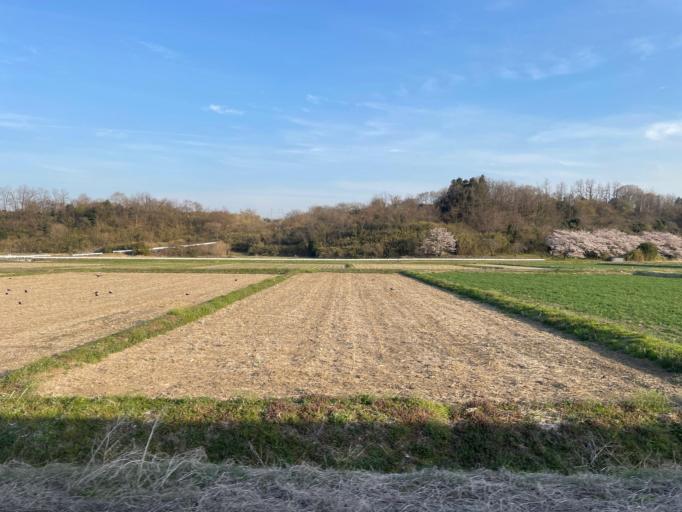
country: JP
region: Gunma
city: Annaka
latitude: 36.3067
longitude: 138.8745
